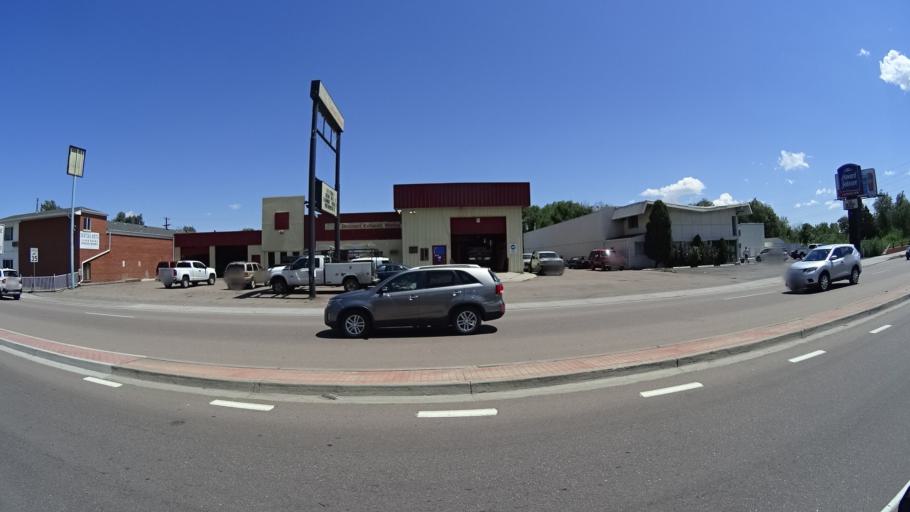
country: US
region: Colorado
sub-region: El Paso County
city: Colorado Springs
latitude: 38.8170
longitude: -104.8225
